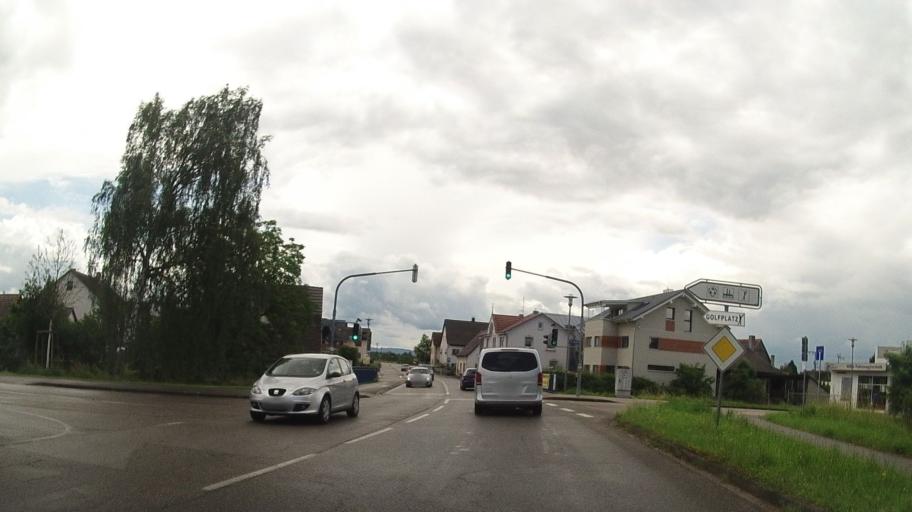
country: DE
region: Baden-Wuerttemberg
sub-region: Freiburg Region
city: Appenweier
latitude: 48.5570
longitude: 7.9794
